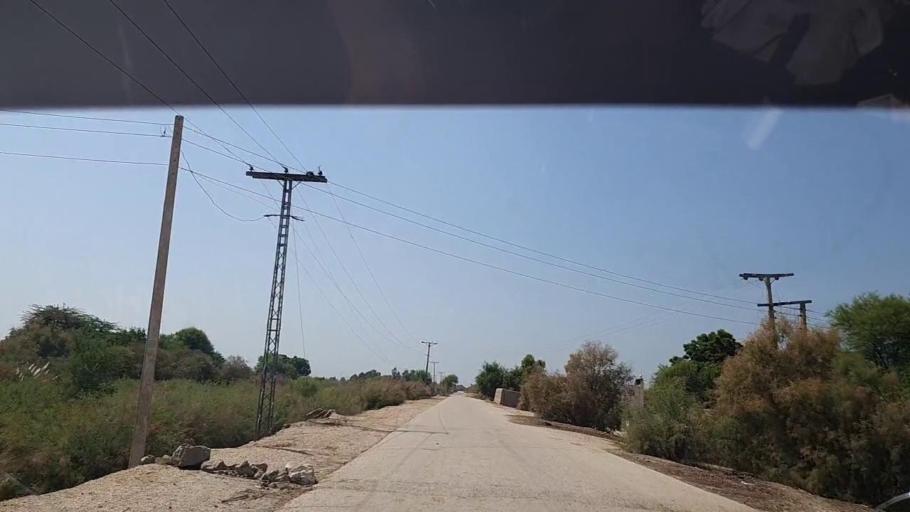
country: PK
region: Sindh
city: Ghauspur
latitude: 28.1573
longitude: 69.1509
